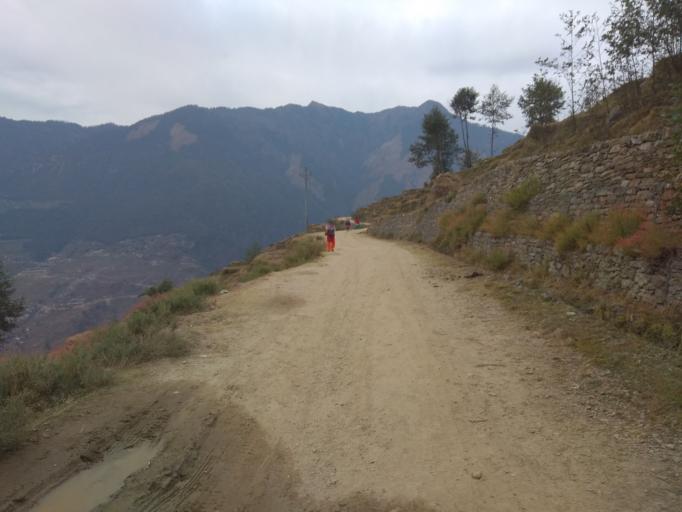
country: NP
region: Far Western
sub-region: Seti Zone
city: Achham
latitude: 29.2570
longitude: 81.6314
